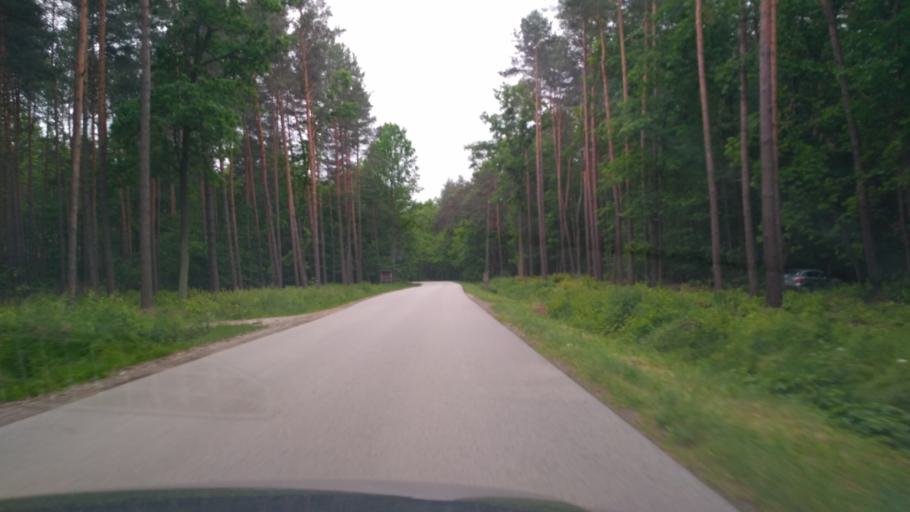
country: PL
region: Subcarpathian Voivodeship
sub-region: Powiat ropczycko-sedziszowski
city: Sedziszow Malopolski
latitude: 50.1281
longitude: 21.6715
